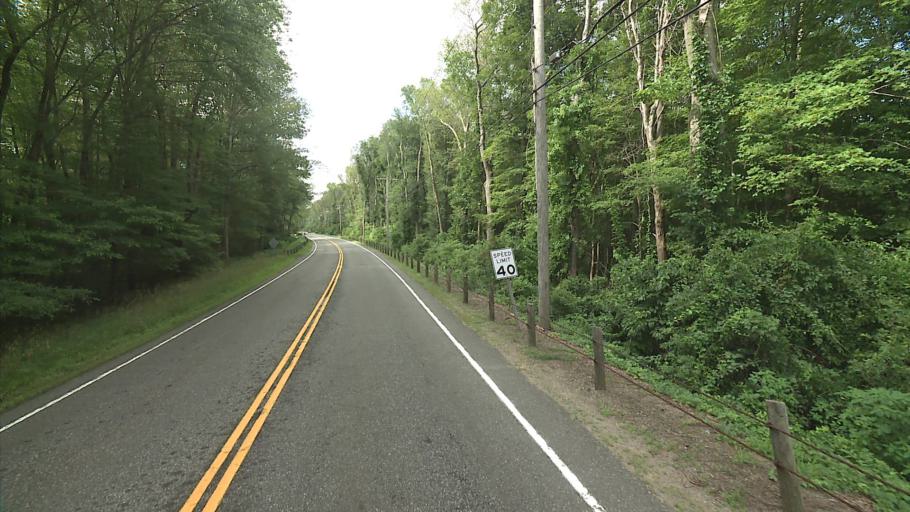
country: US
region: Connecticut
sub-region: Middlesex County
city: Chester Center
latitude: 41.3866
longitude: -72.5085
